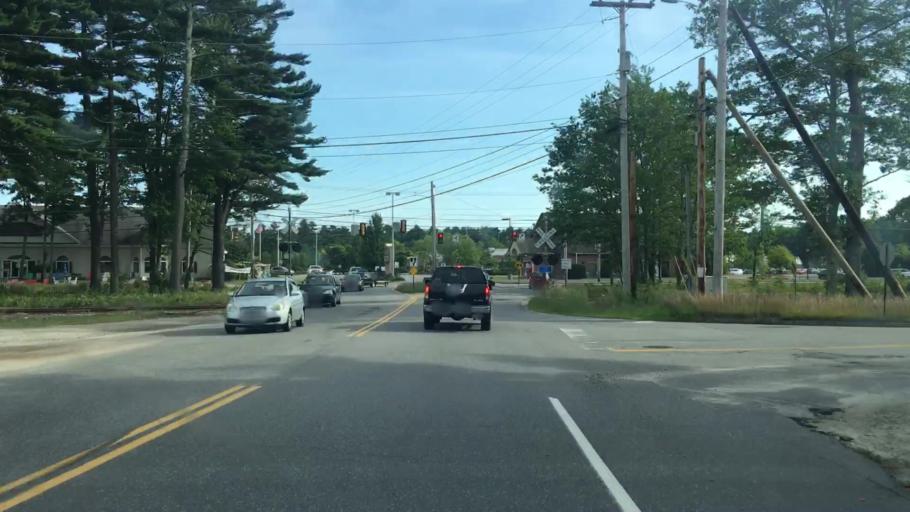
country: US
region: Maine
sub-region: Cumberland County
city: Brunswick
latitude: 43.9105
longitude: -69.9074
